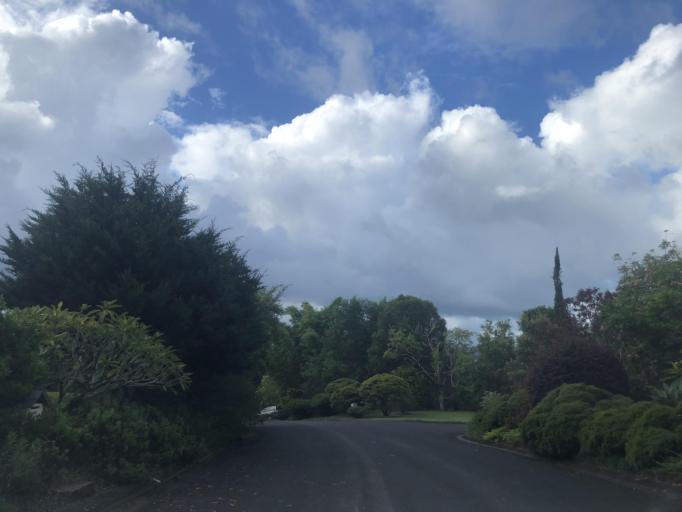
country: AU
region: New South Wales
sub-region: Bellingen
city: Bellingen
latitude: -30.4612
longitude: 152.9023
